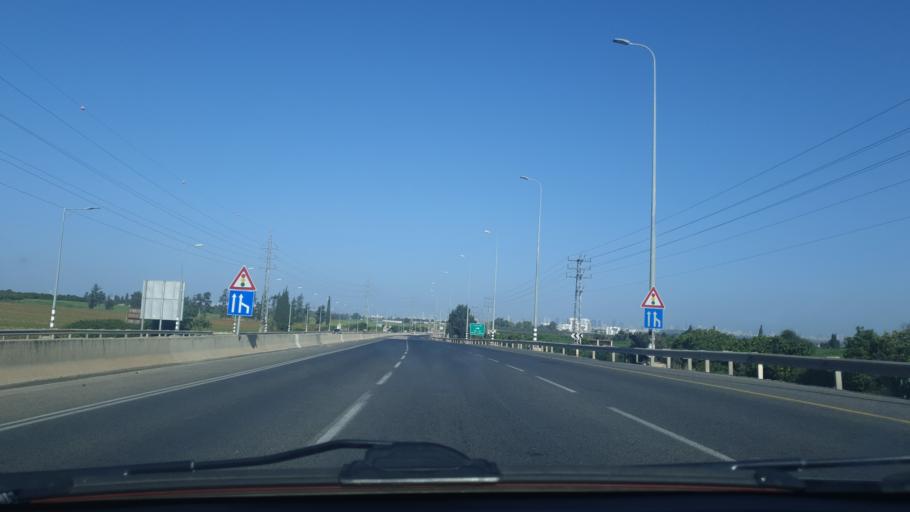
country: IL
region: Central District
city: Kefar Habad
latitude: 31.9758
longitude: 34.8394
